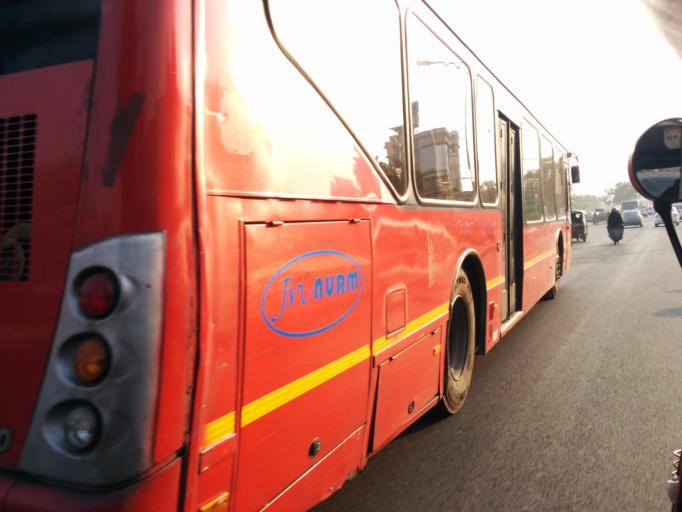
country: IN
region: Rajasthan
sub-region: Jaipur
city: Jaipur
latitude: 26.9598
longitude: 75.8448
